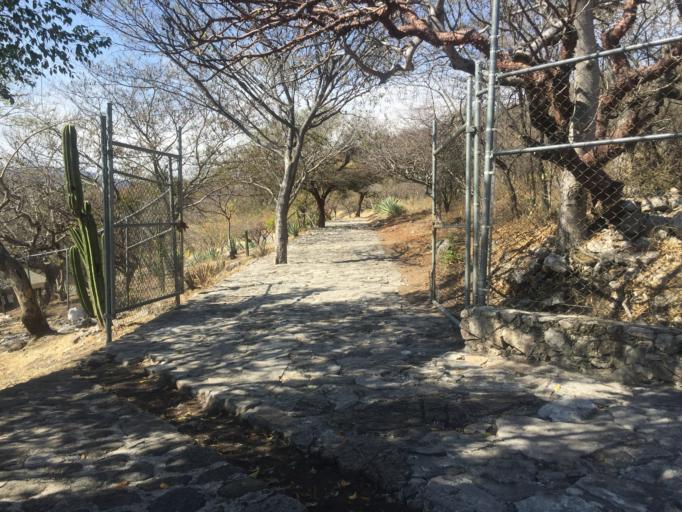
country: MX
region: Morelos
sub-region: Miacatlan
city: Xochicalco (Cirenio Longares)
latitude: 18.8027
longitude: -99.2912
